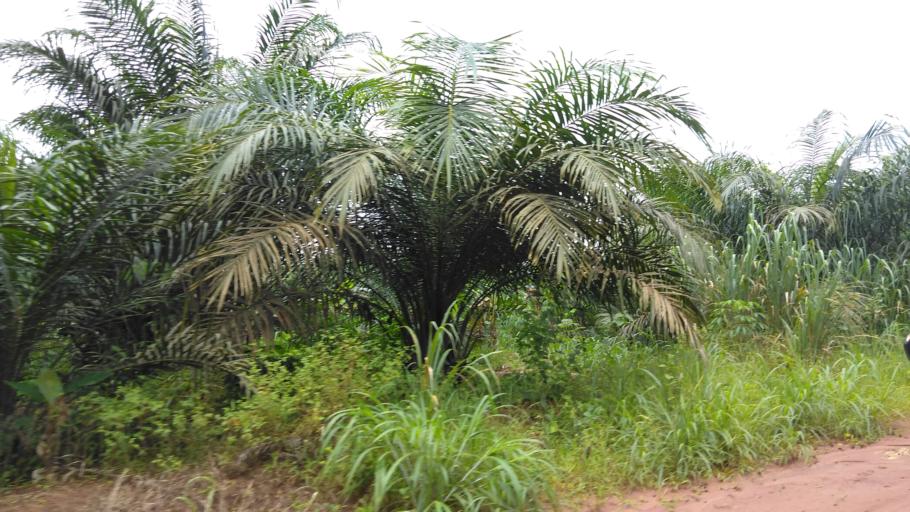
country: NG
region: Ogun
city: Abigi
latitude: 6.5842
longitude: 4.5581
